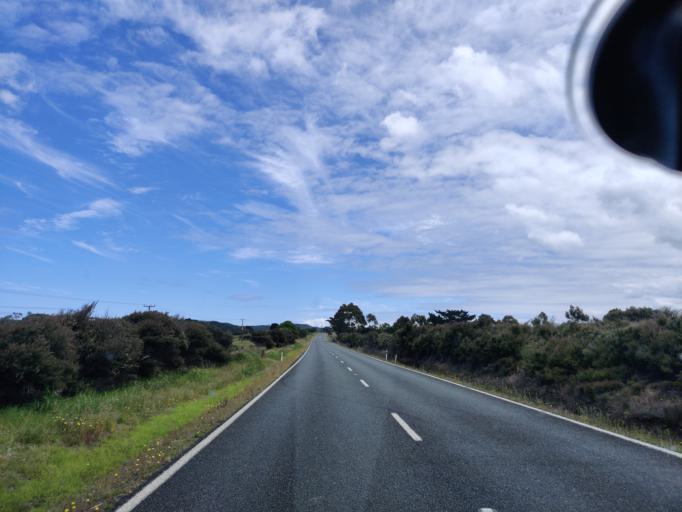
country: NZ
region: Northland
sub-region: Far North District
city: Kaitaia
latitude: -34.6724
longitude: 172.9939
